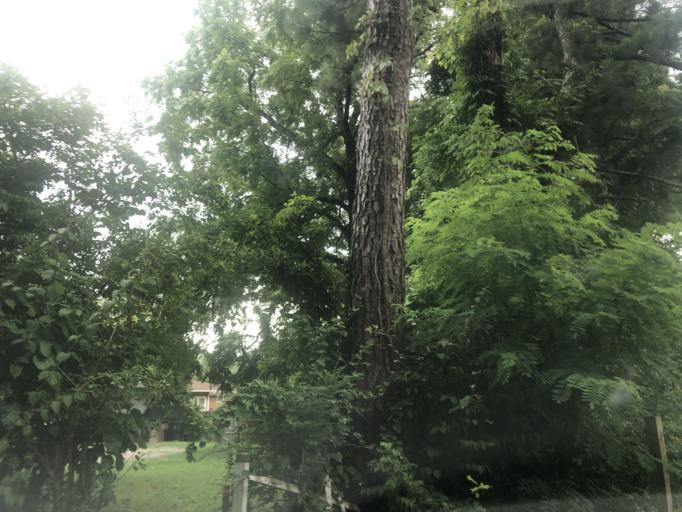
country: US
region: Tennessee
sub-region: Davidson County
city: Nashville
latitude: 36.1612
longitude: -86.6878
